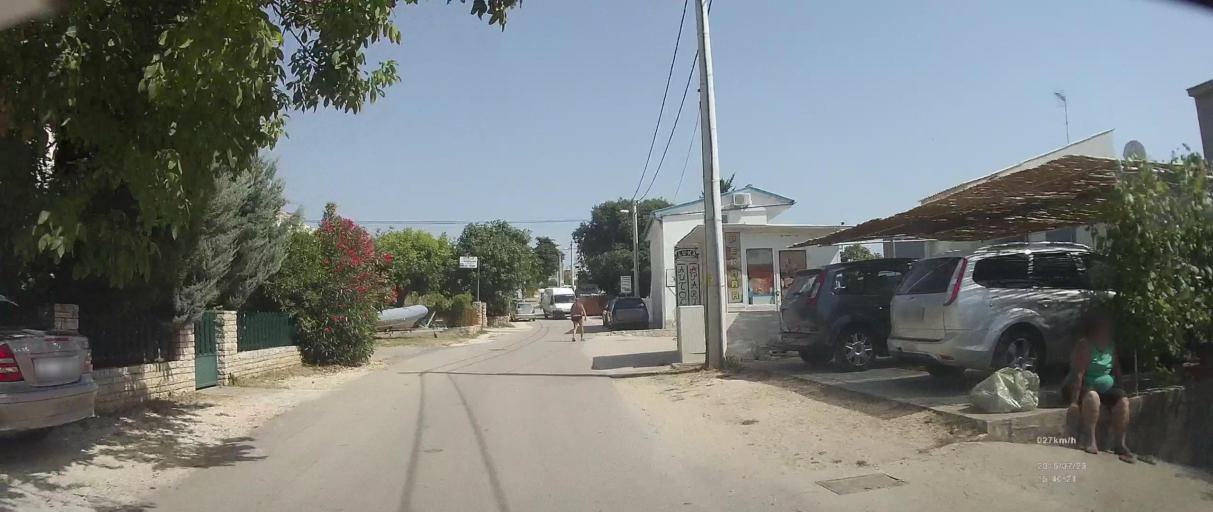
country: HR
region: Zadarska
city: Pakostane
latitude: 43.9060
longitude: 15.5158
